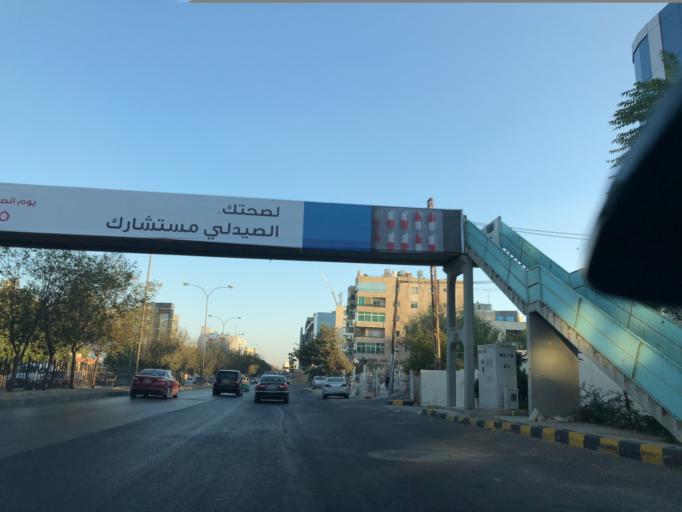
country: JO
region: Amman
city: Wadi as Sir
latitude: 31.9671
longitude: 35.8422
